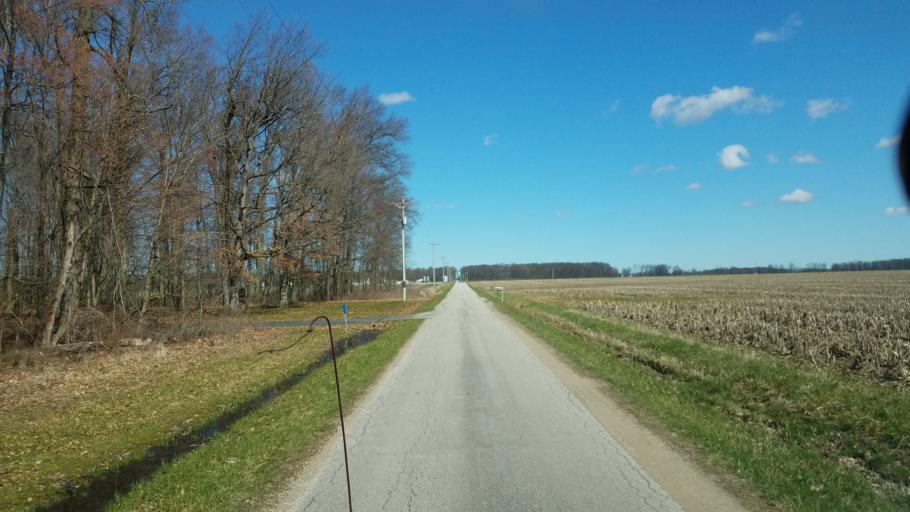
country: US
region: Ohio
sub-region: Sandusky County
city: Mount Carmel
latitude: 41.2364
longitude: -82.9370
